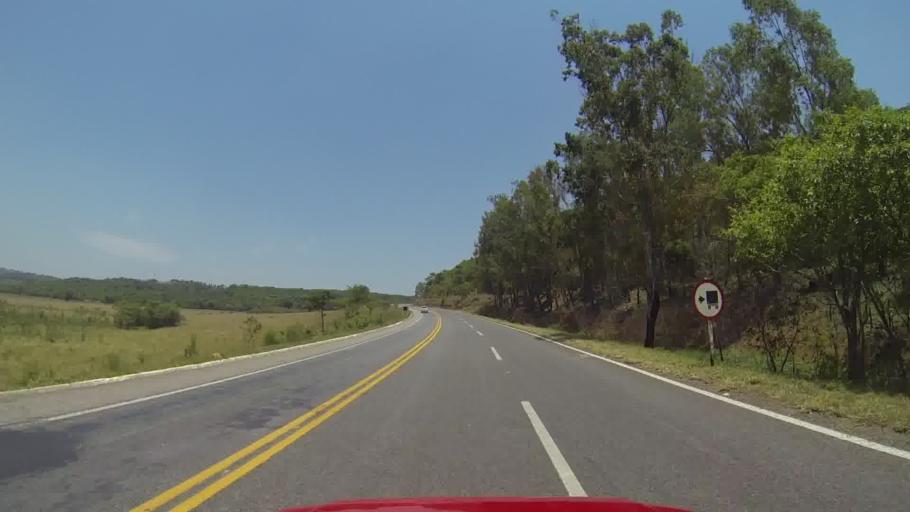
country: BR
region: Minas Gerais
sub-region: Itapecerica
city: Itapecerica
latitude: -20.2846
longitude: -45.1491
